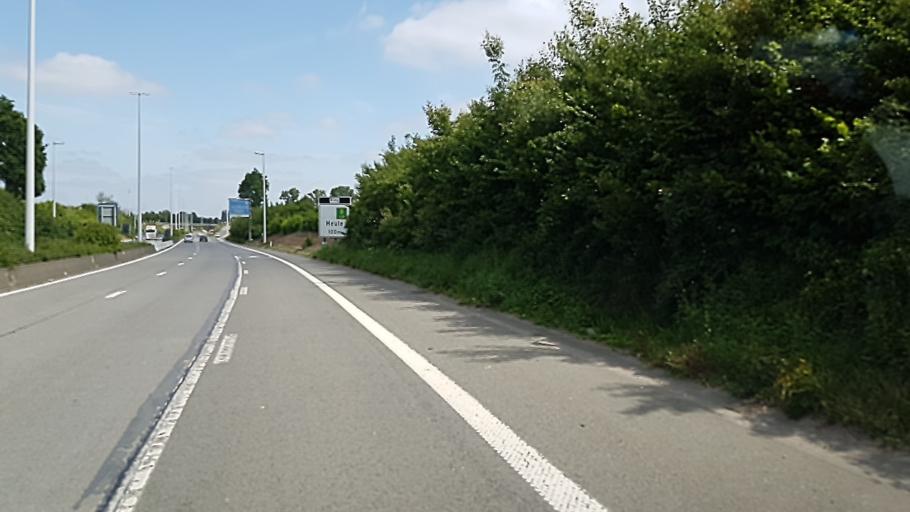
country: BE
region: Flanders
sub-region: Provincie West-Vlaanderen
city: Kortrijk
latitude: 50.8389
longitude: 3.2232
